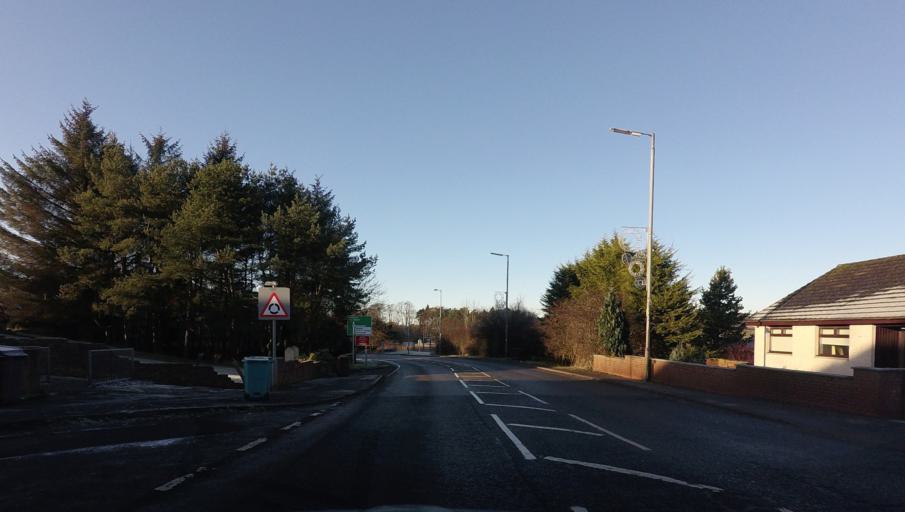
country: GB
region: Scotland
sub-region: North Lanarkshire
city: Shotts
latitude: 55.8003
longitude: -3.8380
